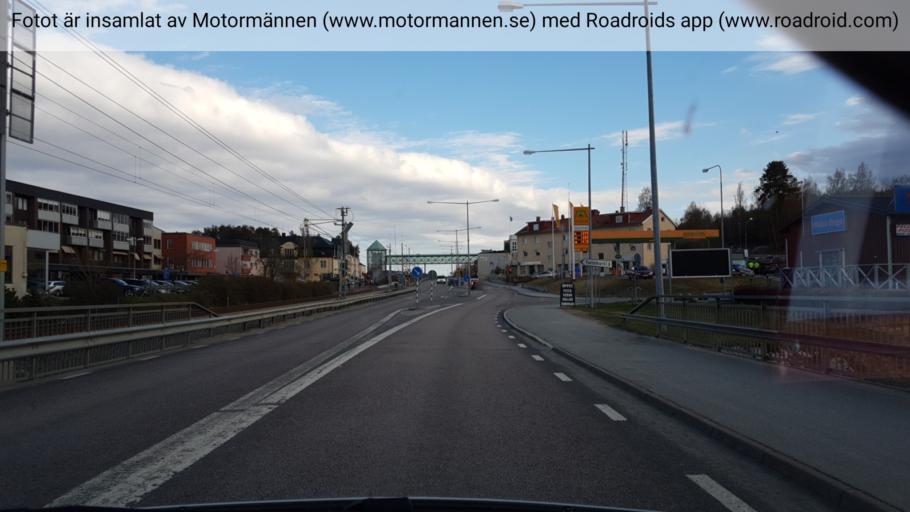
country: SE
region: Vaesternorrland
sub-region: Kramfors Kommun
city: Kramfors
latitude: 62.9325
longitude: 17.7736
